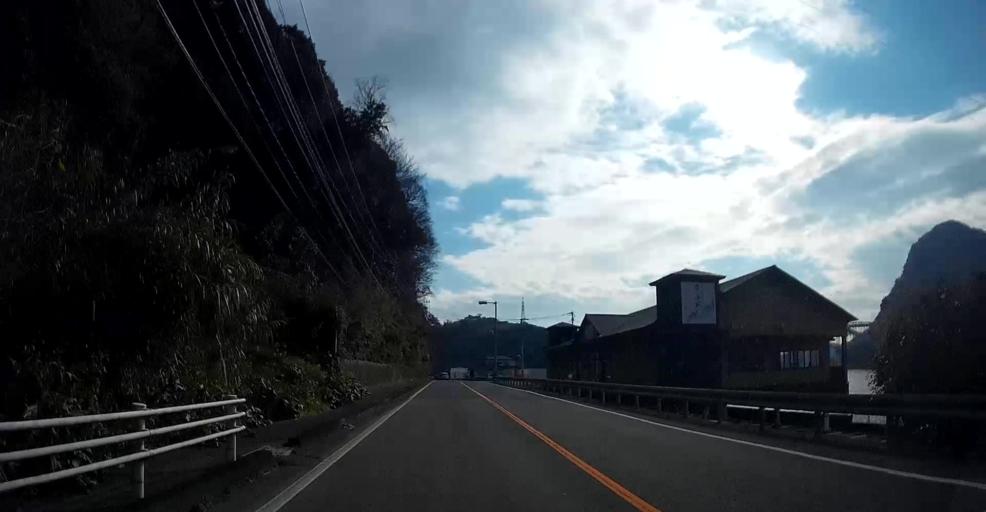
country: JP
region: Kumamoto
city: Yatsushiro
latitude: 32.6166
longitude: 130.4620
